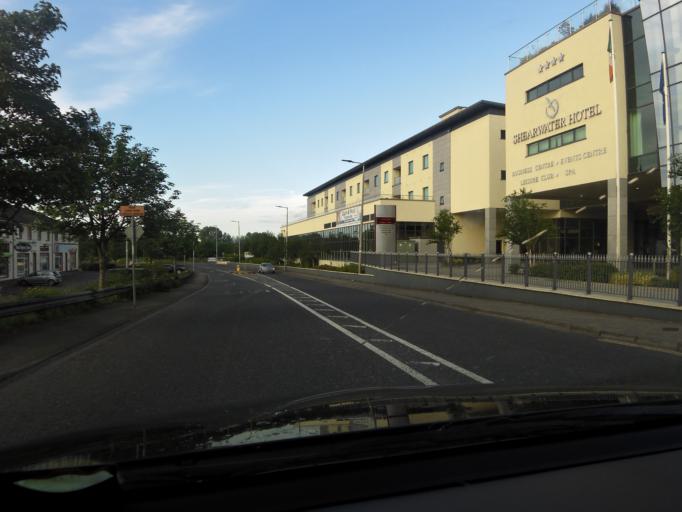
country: IE
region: Connaught
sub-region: County Galway
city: Ballinasloe
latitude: 53.3265
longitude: -8.2206
